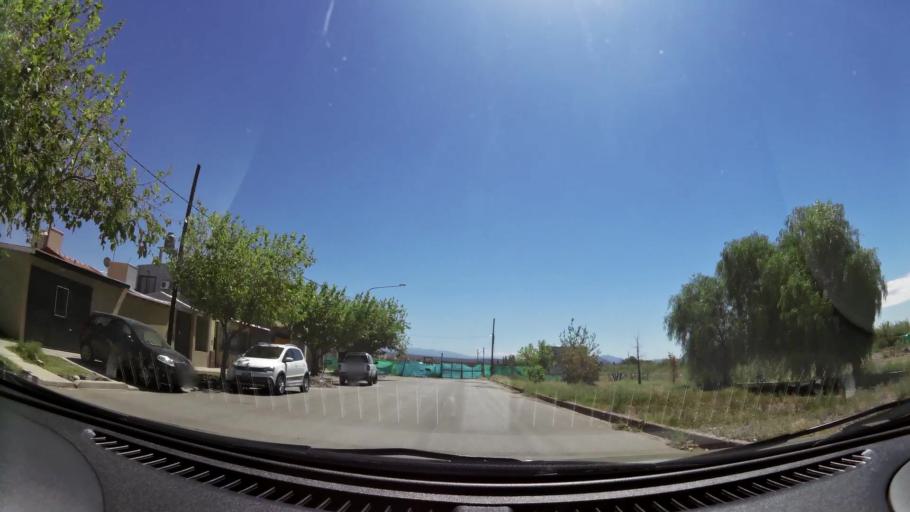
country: AR
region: Mendoza
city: Las Heras
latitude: -32.8382
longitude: -68.8629
